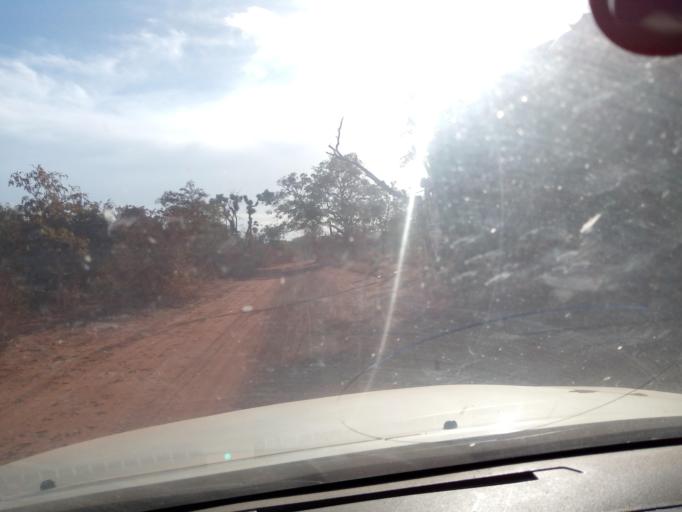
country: ML
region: Sikasso
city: Sikasso
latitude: 11.4244
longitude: -5.5612
